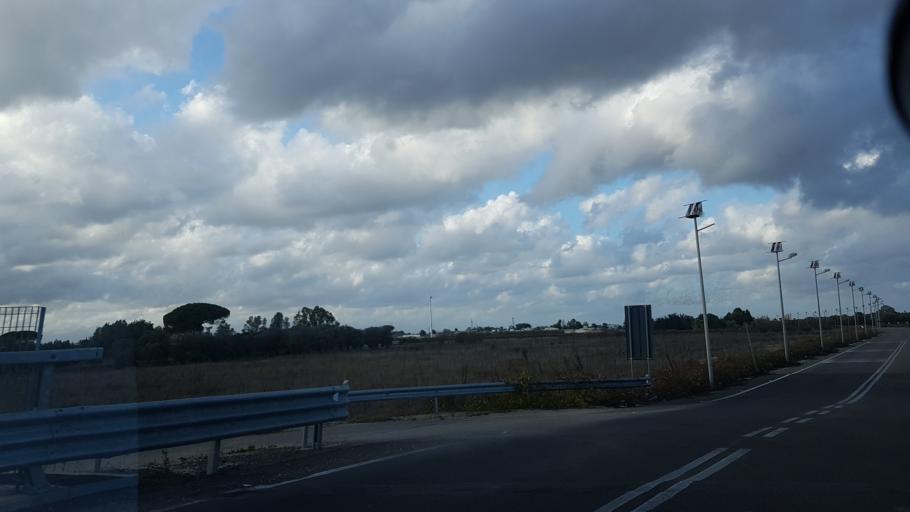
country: IT
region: Apulia
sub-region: Provincia di Brindisi
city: San Pietro Vernotico
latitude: 40.4898
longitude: 18.0106
